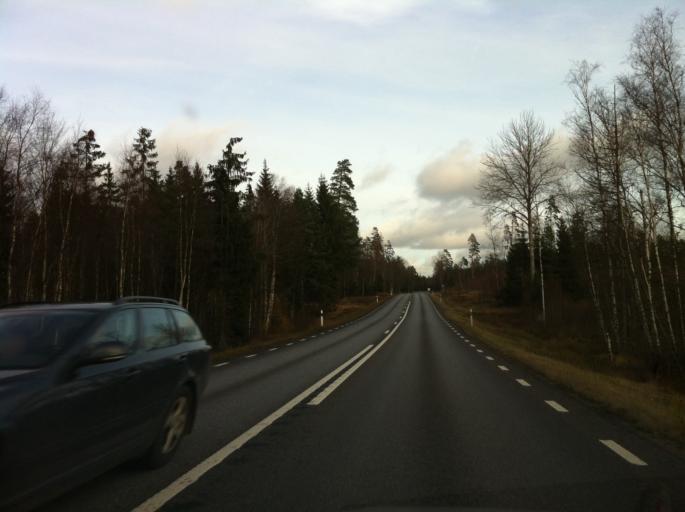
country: SE
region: Kronoberg
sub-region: Alvesta Kommun
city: Vislanda
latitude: 56.7637
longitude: 14.5259
